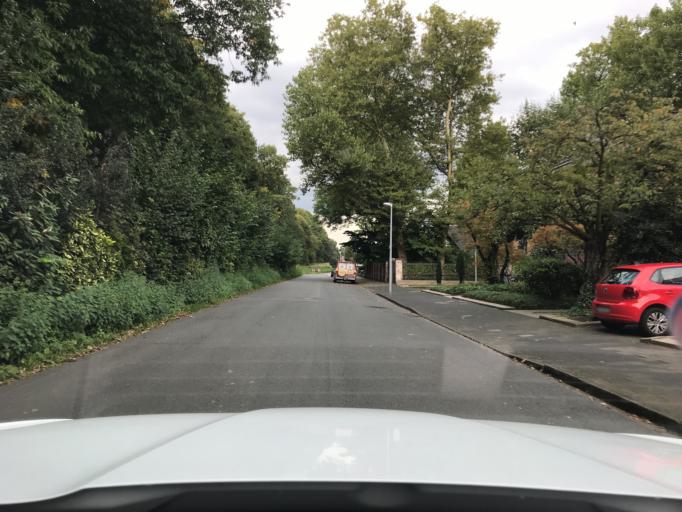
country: DE
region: North Rhine-Westphalia
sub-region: Regierungsbezirk Dusseldorf
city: Duisburg
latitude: 51.4347
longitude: 6.8181
